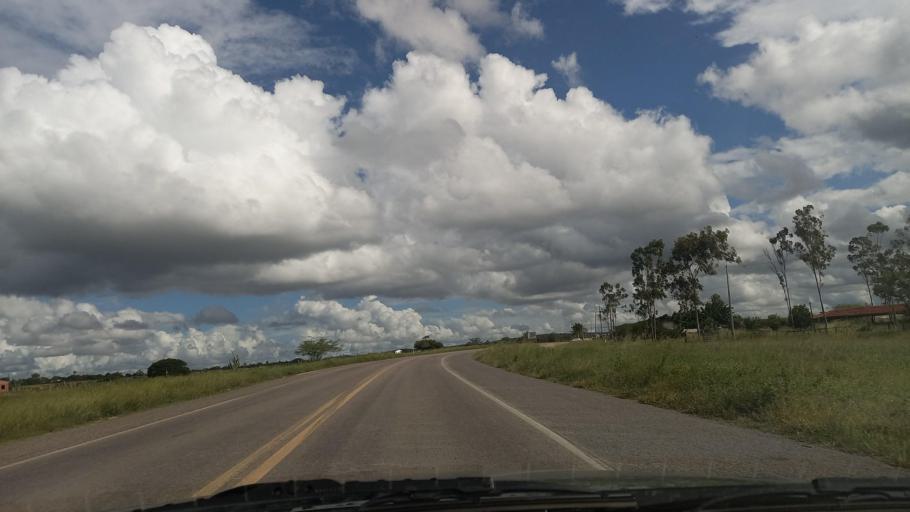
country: BR
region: Pernambuco
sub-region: Lajedo
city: Lajedo
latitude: -8.6301
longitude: -36.3034
